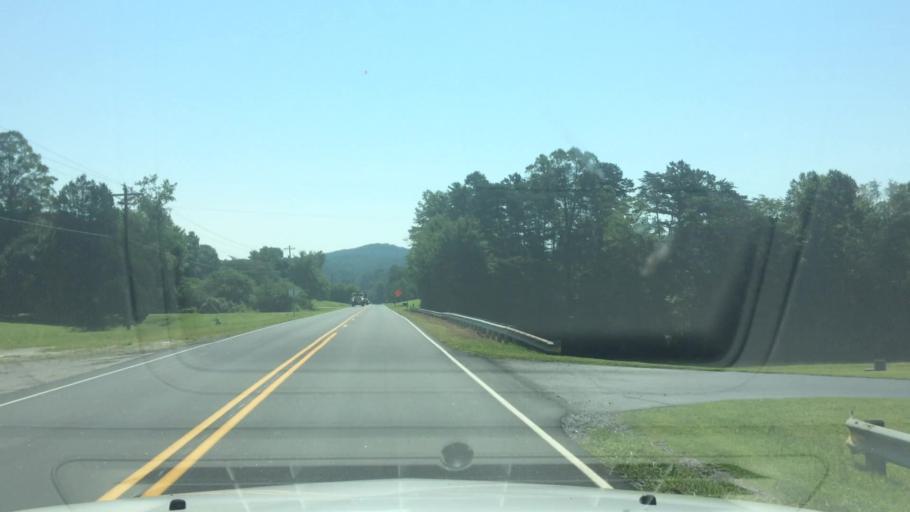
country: US
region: North Carolina
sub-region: Caldwell County
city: Sawmills
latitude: 35.9074
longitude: -81.4014
